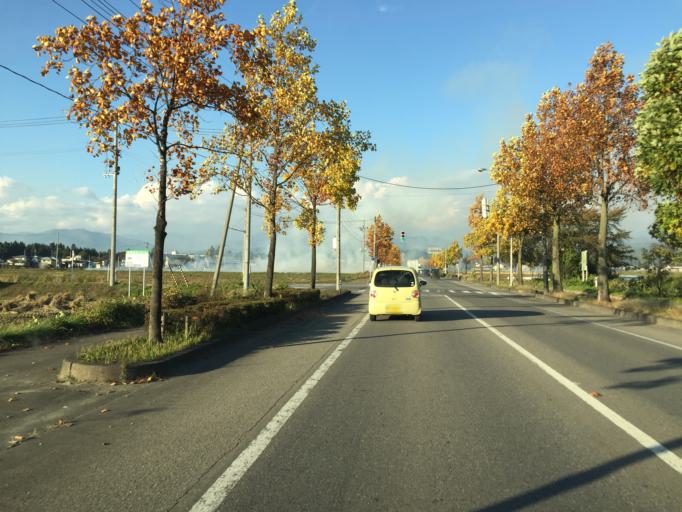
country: JP
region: Fukushima
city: Kitakata
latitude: 37.6623
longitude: 139.8876
